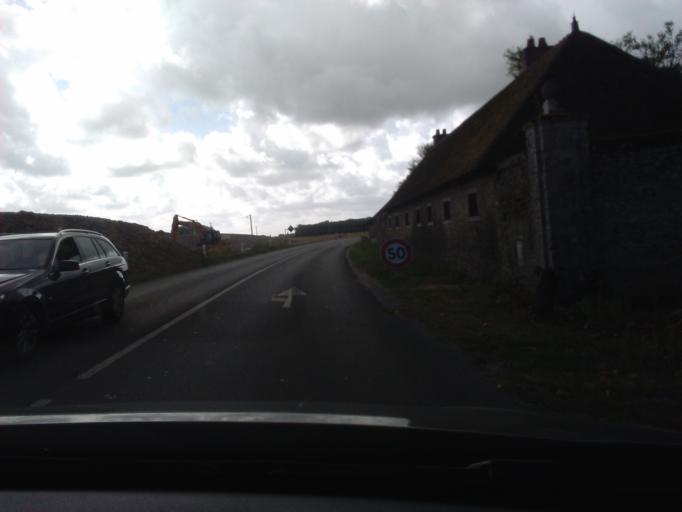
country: FR
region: Centre
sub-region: Departement du Loir-et-Cher
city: Cormeray
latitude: 47.5142
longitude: 1.4009
